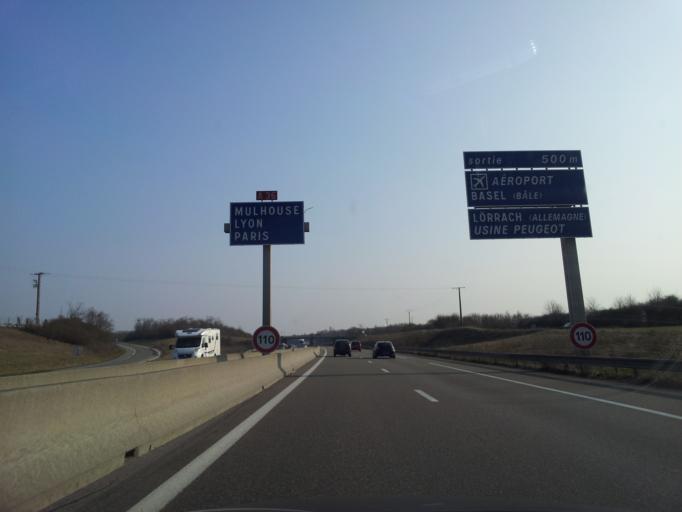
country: FR
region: Alsace
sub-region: Departement du Haut-Rhin
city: Baldersheim
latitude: 47.7964
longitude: 7.3949
